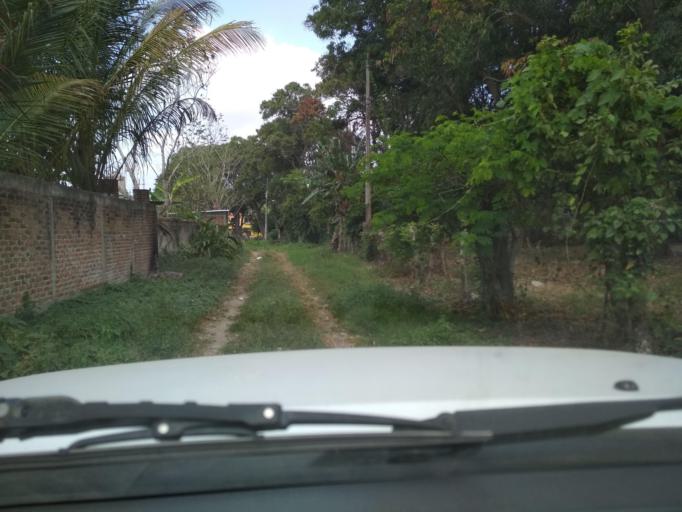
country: MX
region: Veracruz
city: El Tejar
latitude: 19.0793
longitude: -96.1727
